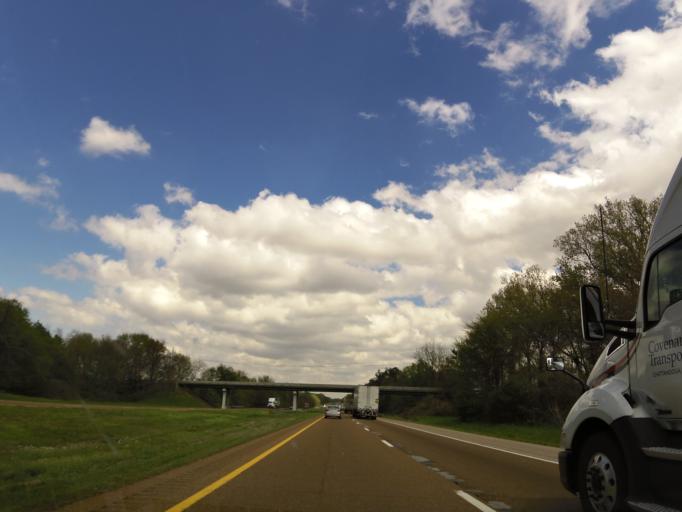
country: US
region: Tennessee
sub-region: Tipton County
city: Mason
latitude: 35.3627
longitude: -89.4881
